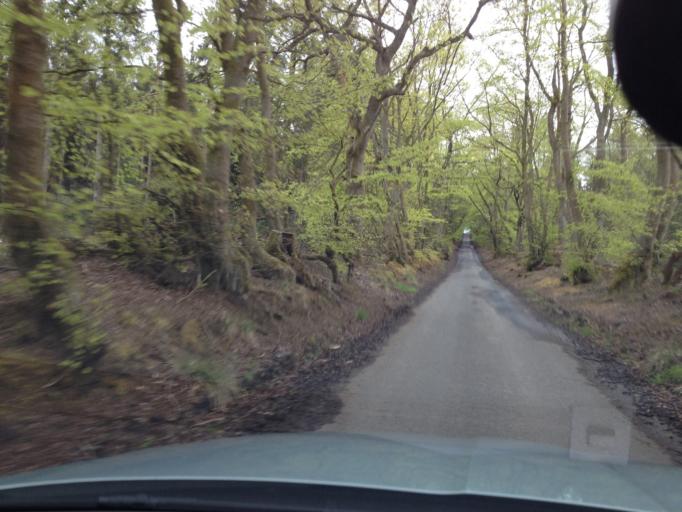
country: GB
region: Scotland
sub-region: West Lothian
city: Linlithgow
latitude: 55.9452
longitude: -3.6047
